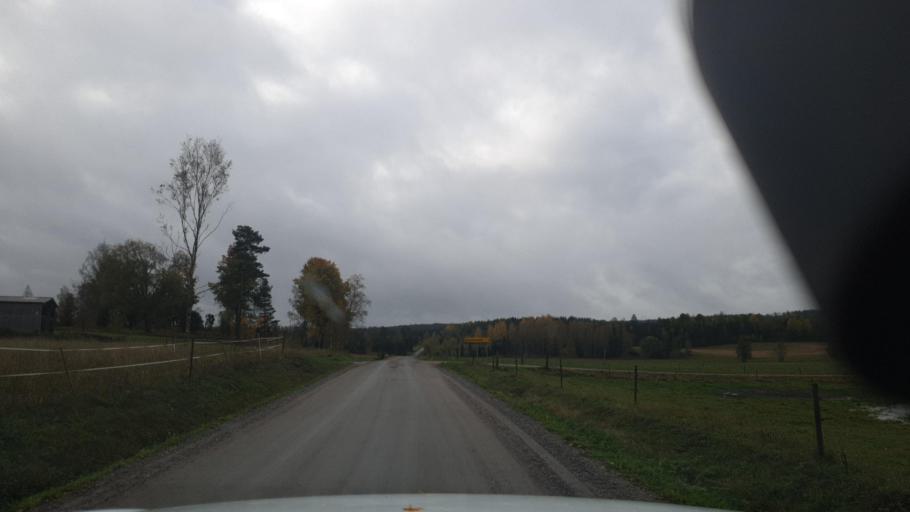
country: SE
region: Vaermland
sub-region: Karlstads Kommun
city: Edsvalla
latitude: 59.5557
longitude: 13.0125
